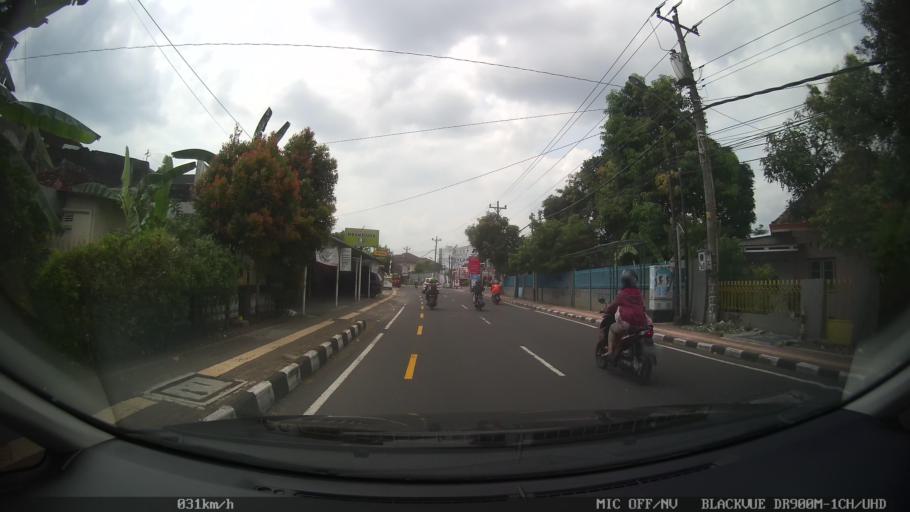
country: ID
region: Daerah Istimewa Yogyakarta
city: Yogyakarta
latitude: -7.7859
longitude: 110.3874
